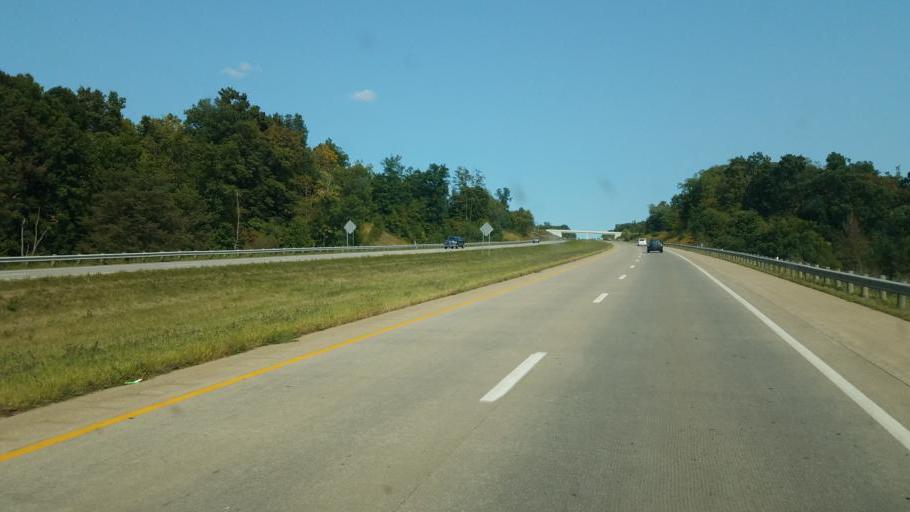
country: US
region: Ohio
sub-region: Wayne County
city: Wooster
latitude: 40.7988
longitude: -81.8855
